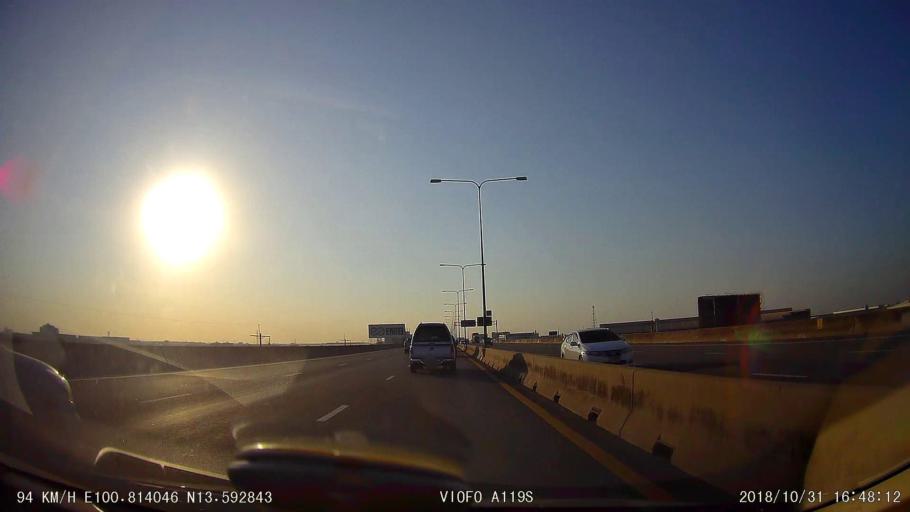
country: TH
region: Samut Prakan
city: Bang Bo District
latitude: 13.5927
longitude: 100.8142
